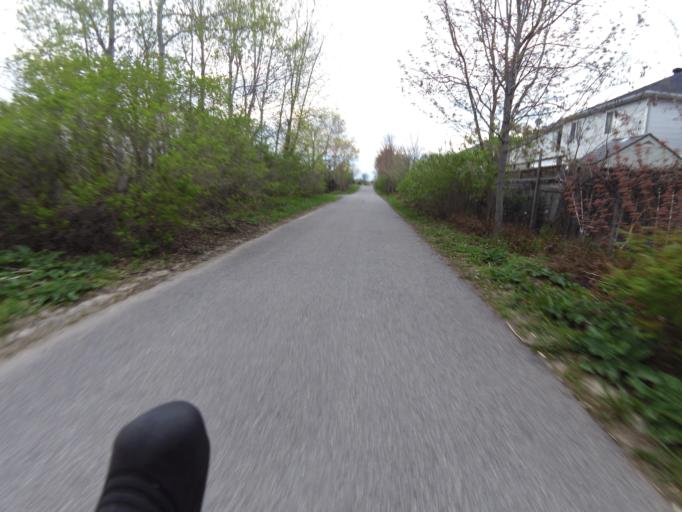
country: CA
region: Ontario
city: Bells Corners
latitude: 45.2774
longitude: -75.7474
